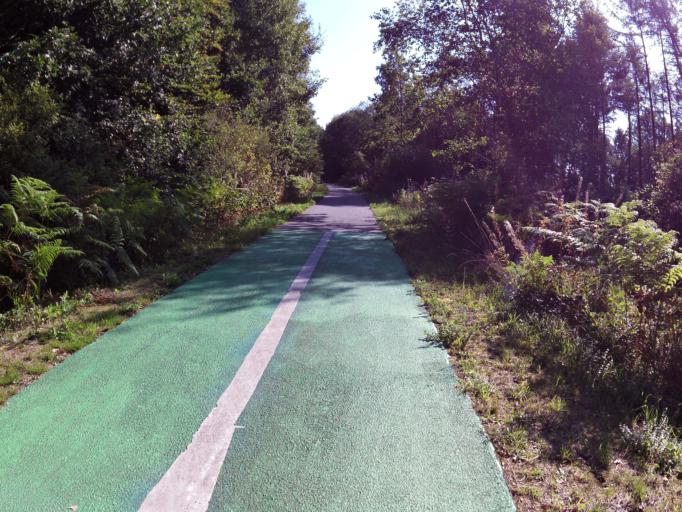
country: BE
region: Wallonia
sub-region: Province de Liege
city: Butgenbach
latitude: 50.4067
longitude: 6.1633
